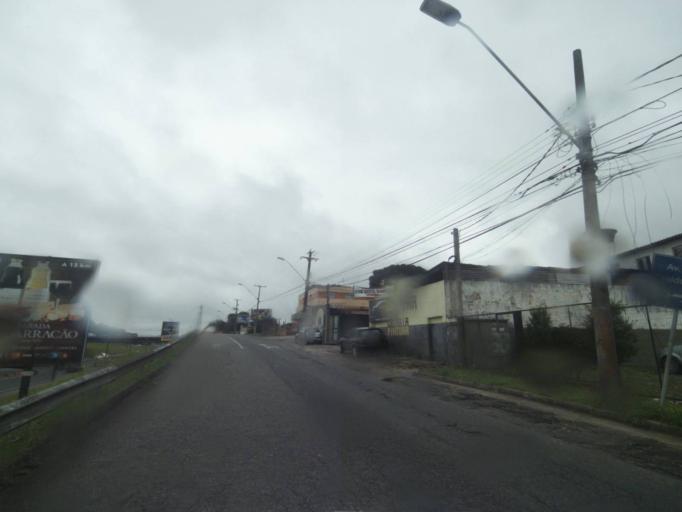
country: BR
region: Parana
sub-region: Curitiba
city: Curitiba
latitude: -25.4301
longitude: -49.3514
